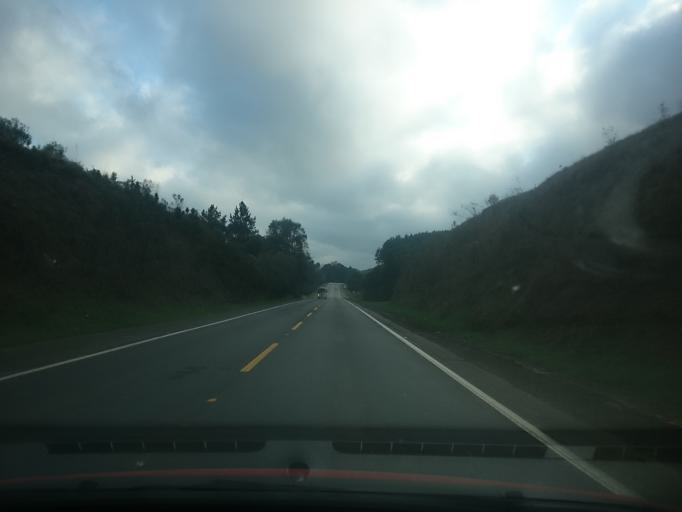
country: BR
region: Santa Catarina
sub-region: Lages
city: Lages
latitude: -27.9143
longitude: -50.4484
